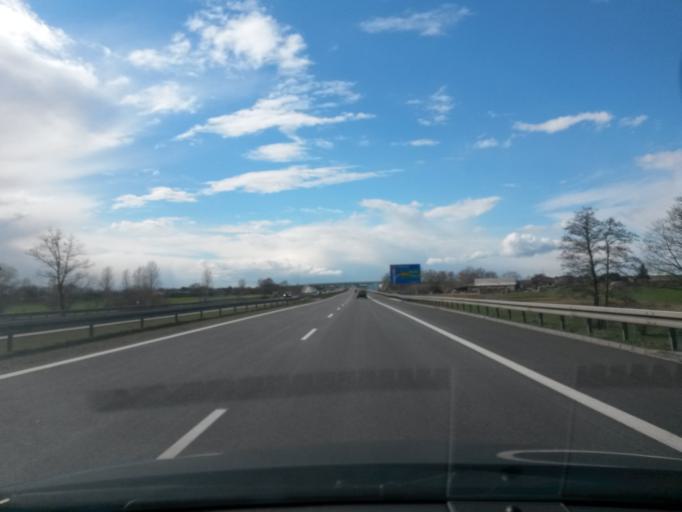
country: PL
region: Greater Poland Voivodeship
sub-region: Powiat slupecki
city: Slupca
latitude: 52.2476
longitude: 17.8507
